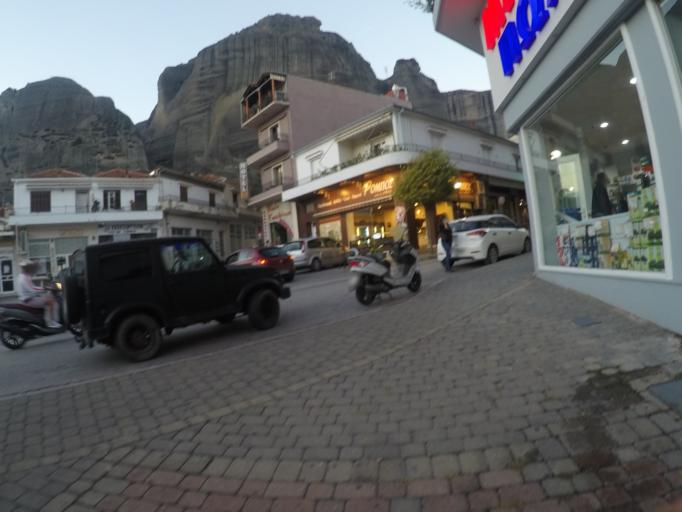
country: GR
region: Thessaly
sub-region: Trikala
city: Kalampaka
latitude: 39.7071
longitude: 21.6238
